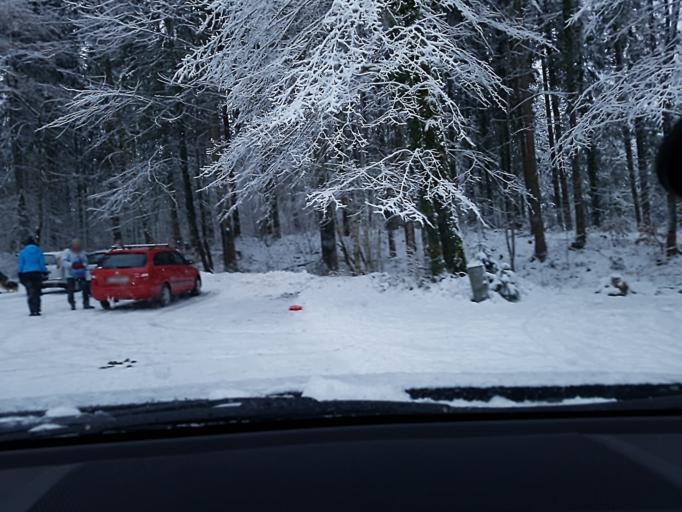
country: DE
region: Bavaria
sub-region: Upper Bavaria
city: Piding
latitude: 47.7359
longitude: 12.9481
